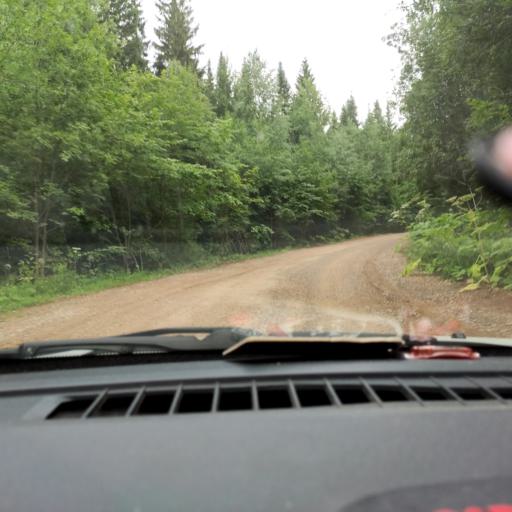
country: RU
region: Perm
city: Kultayevo
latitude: 57.8072
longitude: 56.0040
